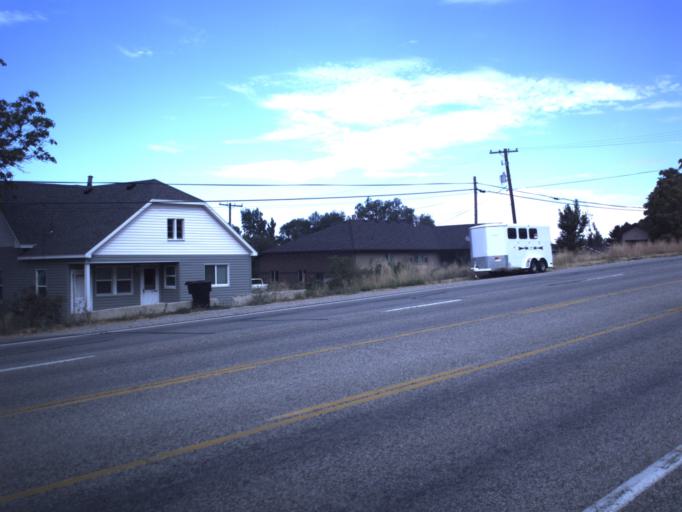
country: US
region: Utah
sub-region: Box Elder County
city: Willard
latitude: 41.4364
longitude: -112.0360
